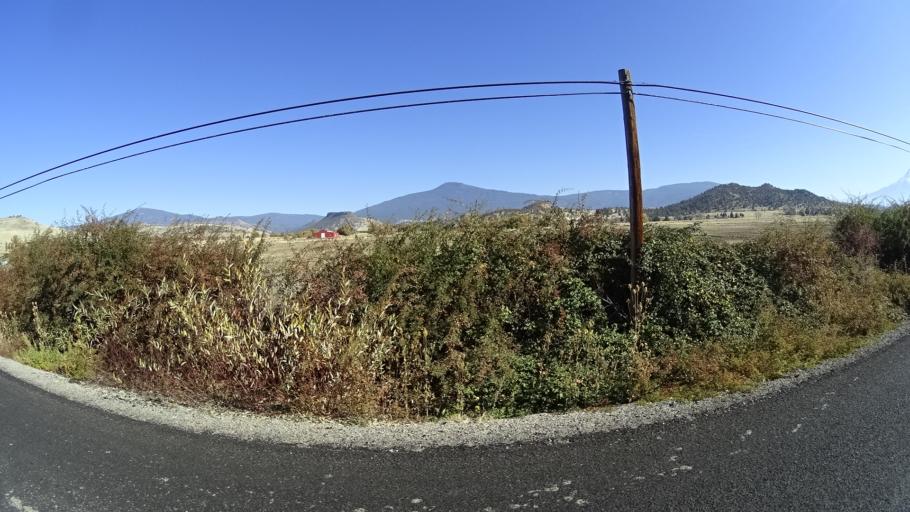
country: US
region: California
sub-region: Siskiyou County
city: Montague
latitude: 41.7214
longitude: -122.3891
